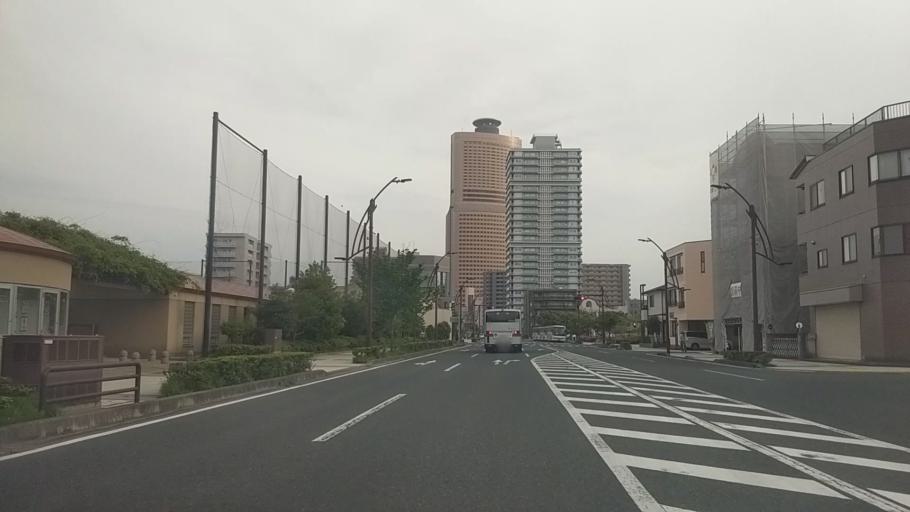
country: JP
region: Shizuoka
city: Hamamatsu
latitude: 34.7119
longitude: 137.7377
